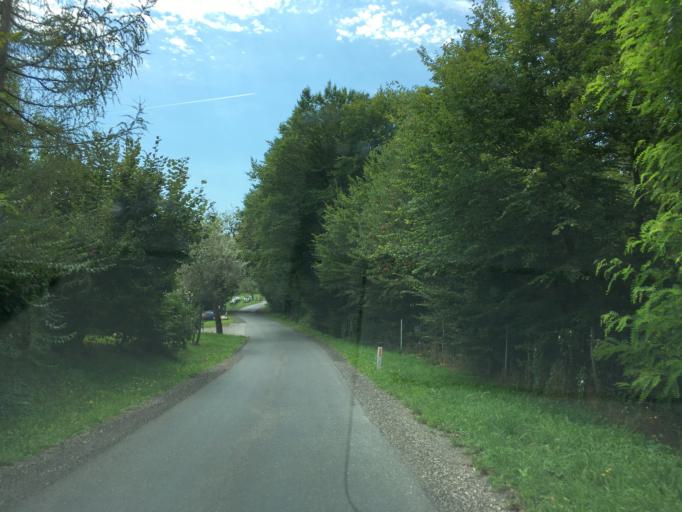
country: AT
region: Styria
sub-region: Politischer Bezirk Leibnitz
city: Pistorf
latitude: 46.7725
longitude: 15.3936
